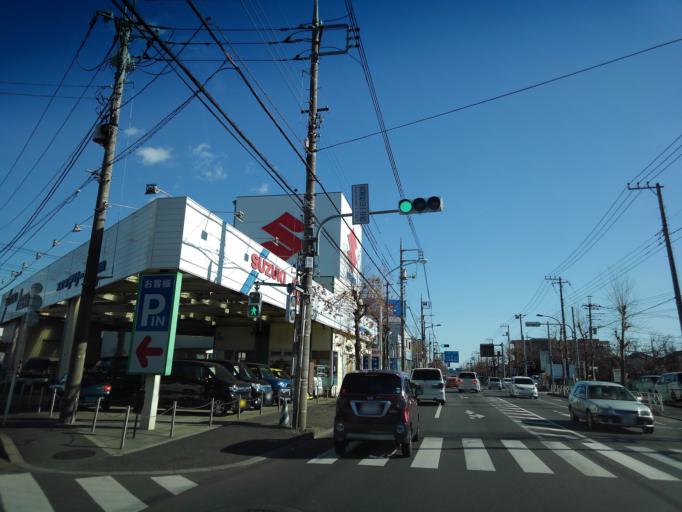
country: JP
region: Tokyo
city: Fussa
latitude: 35.7530
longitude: 139.3805
